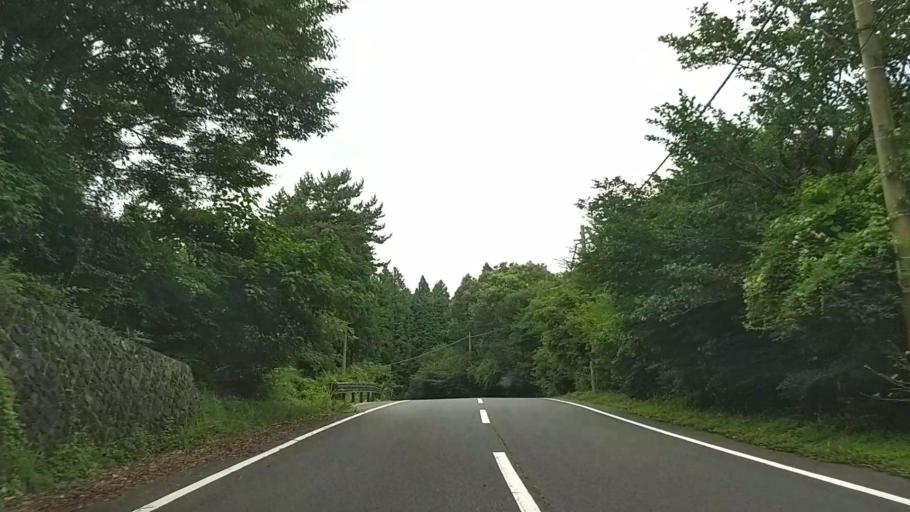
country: JP
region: Shizuoka
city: Gotemba
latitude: 35.3212
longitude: 139.0105
